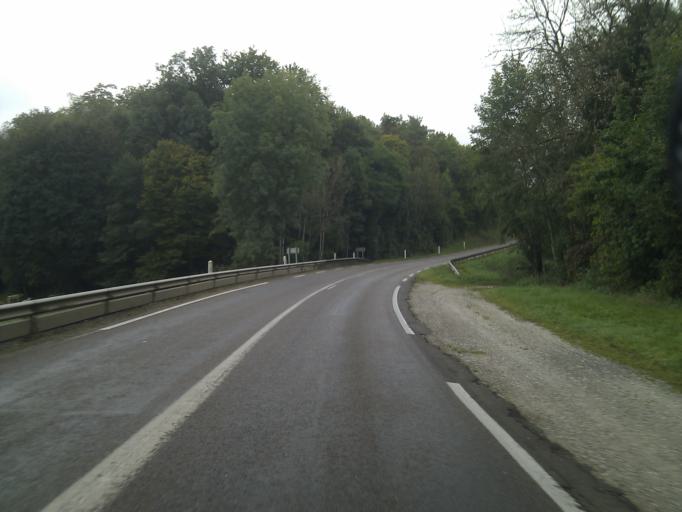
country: FR
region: Champagne-Ardenne
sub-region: Departement de la Haute-Marne
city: Doulaincourt-Saucourt
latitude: 48.2407
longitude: 5.2931
